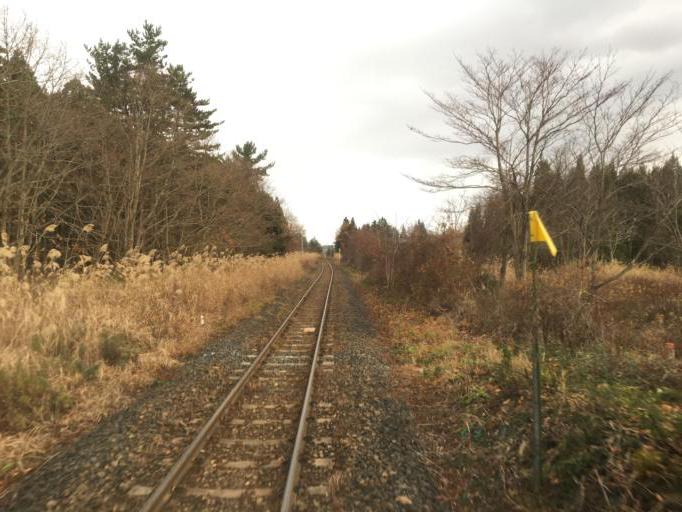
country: JP
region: Aomori
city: Mutsu
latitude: 41.1919
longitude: 141.2791
